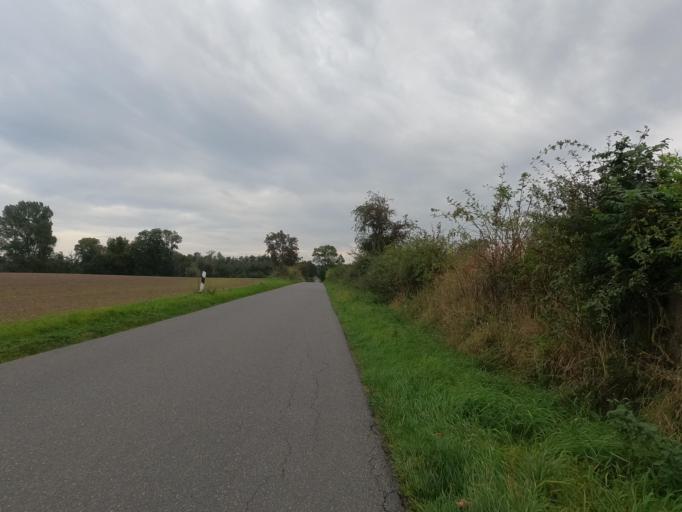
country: DE
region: Schleswig-Holstein
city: Neukirchen
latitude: 54.3055
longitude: 11.0452
